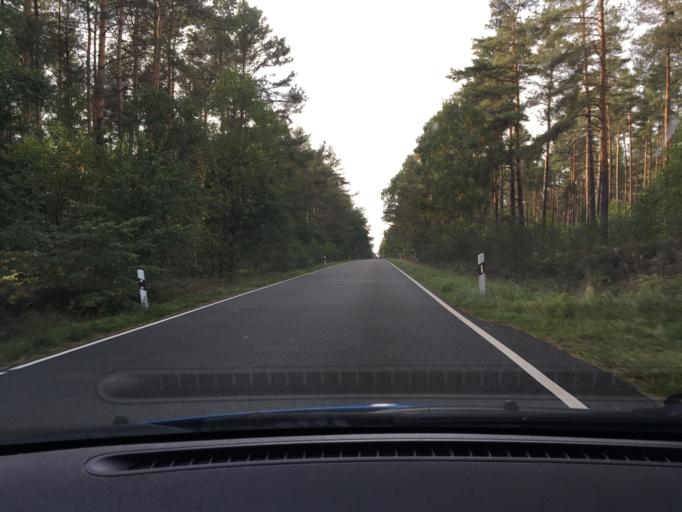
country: DE
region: Lower Saxony
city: Fassberg
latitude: 52.9020
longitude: 10.1051
